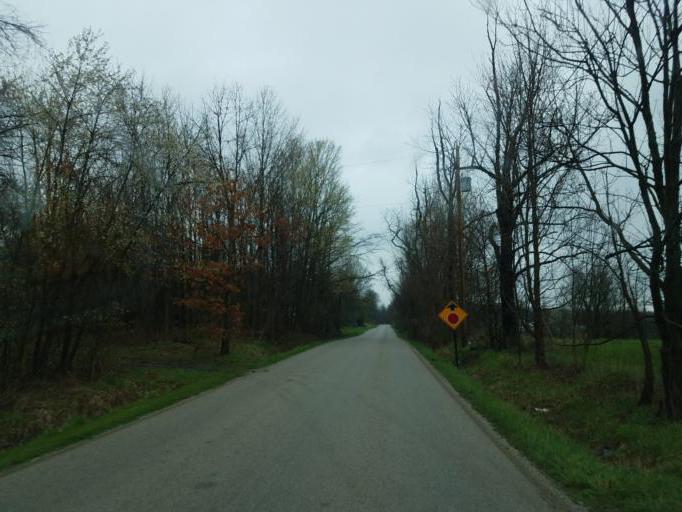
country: US
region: Ohio
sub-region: Morrow County
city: Mount Gilead
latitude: 40.4587
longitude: -82.8069
